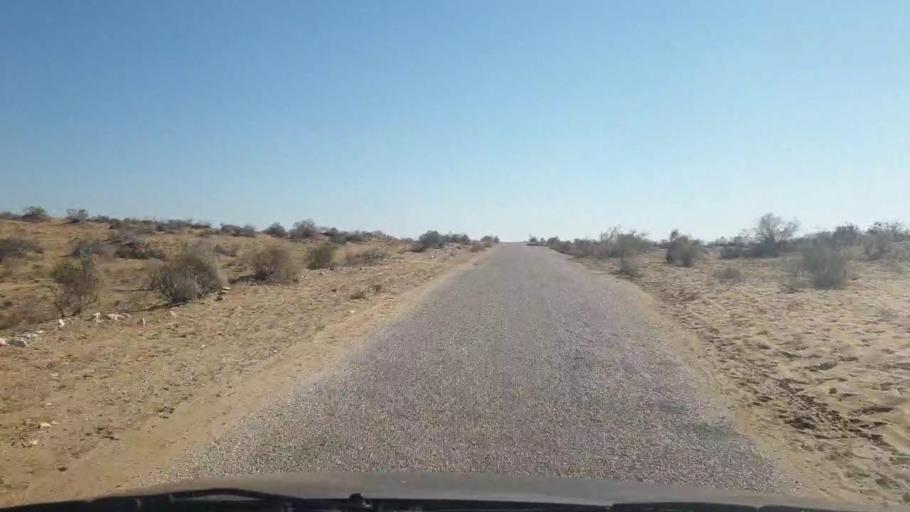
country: PK
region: Sindh
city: Bozdar
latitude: 27.0026
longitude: 68.8068
